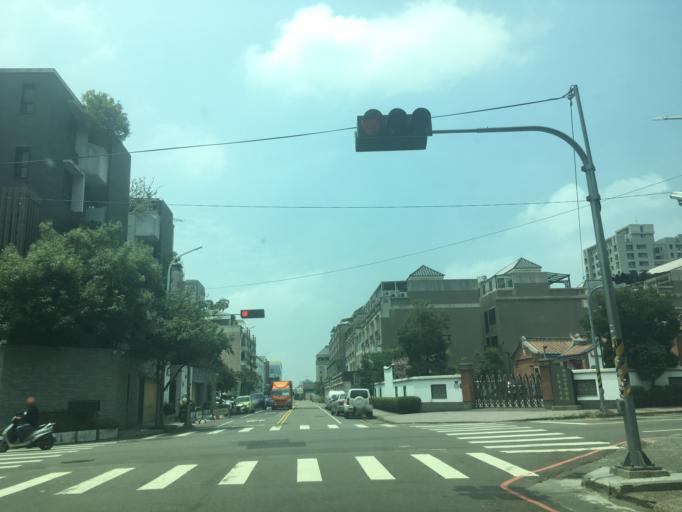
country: TW
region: Taiwan
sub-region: Taichung City
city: Taichung
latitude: 24.1767
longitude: 120.6840
